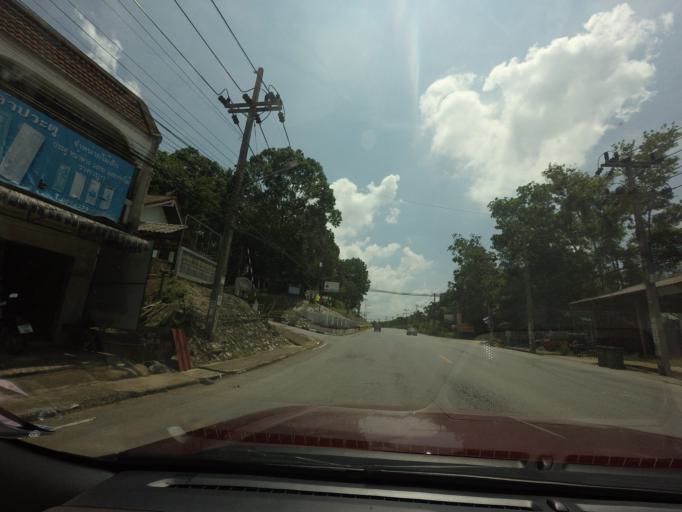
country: TH
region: Yala
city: Betong
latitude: 5.7815
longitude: 101.0738
